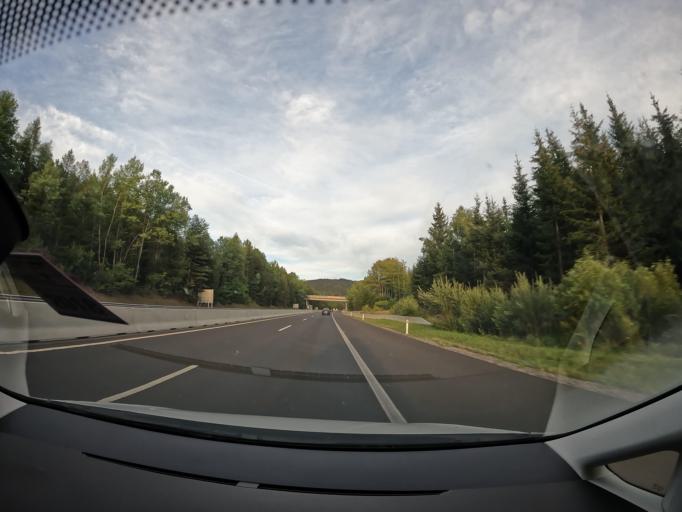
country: AT
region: Carinthia
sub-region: Politischer Bezirk Wolfsberg
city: Preitenegg
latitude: 46.9656
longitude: 14.9503
